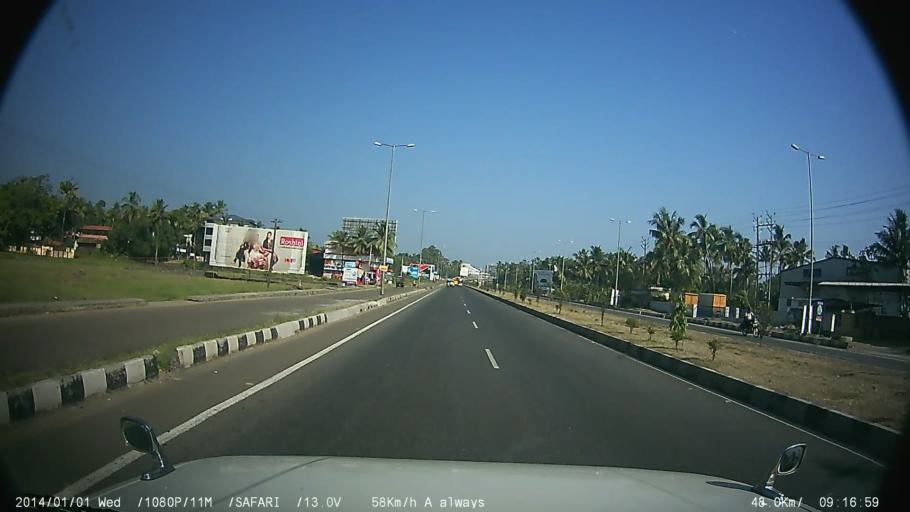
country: IN
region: Kerala
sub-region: Ernakulam
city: Angamali
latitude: 10.2297
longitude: 76.3743
